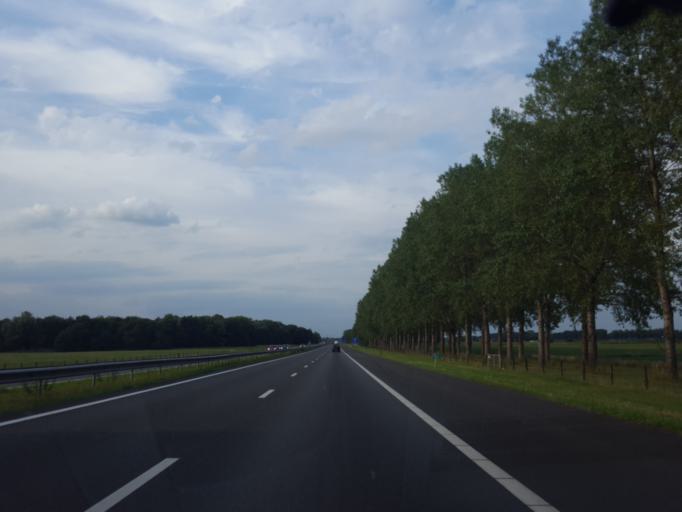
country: NL
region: Gelderland
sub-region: Gemeente Wijchen
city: Bergharen
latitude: 51.8383
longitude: 5.6899
